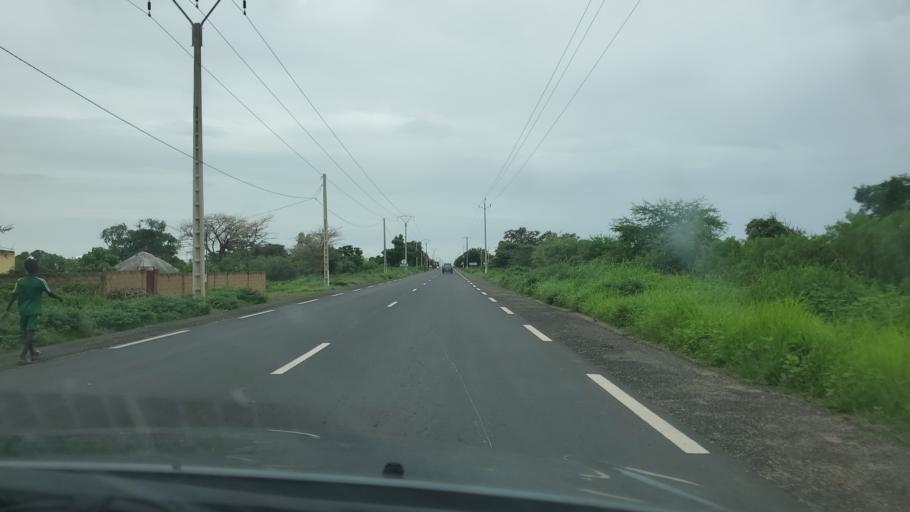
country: SN
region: Thies
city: Kayar
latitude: 15.0606
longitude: -16.9401
